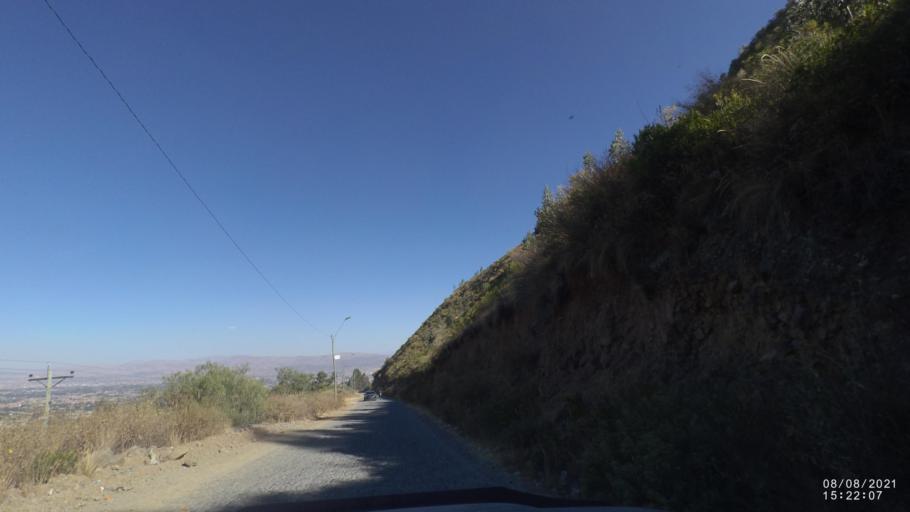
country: BO
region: Cochabamba
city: Cochabamba
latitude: -17.3063
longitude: -66.2944
